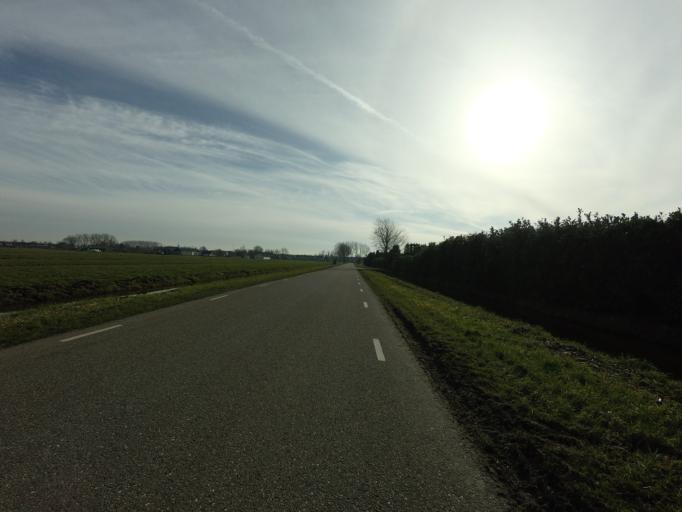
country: NL
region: South Holland
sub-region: Gemeente Hardinxveld-Giessendam
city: Neder-Hardinxveld
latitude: 51.8337
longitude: 4.8262
